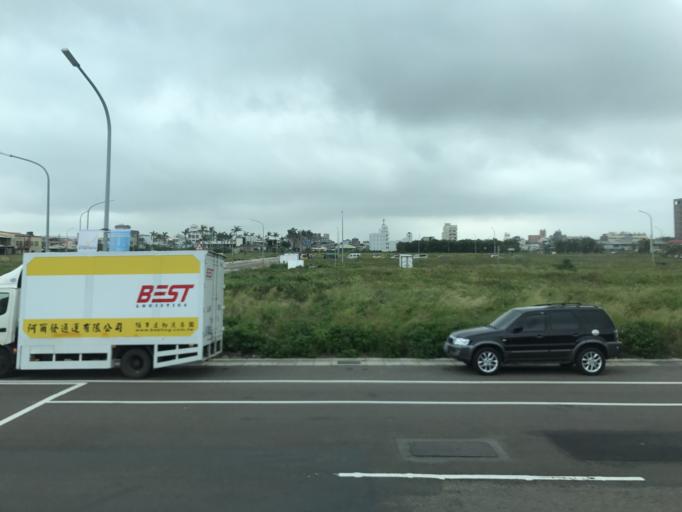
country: TW
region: Taiwan
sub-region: Hsinchu
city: Hsinchu
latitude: 24.8204
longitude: 120.9530
